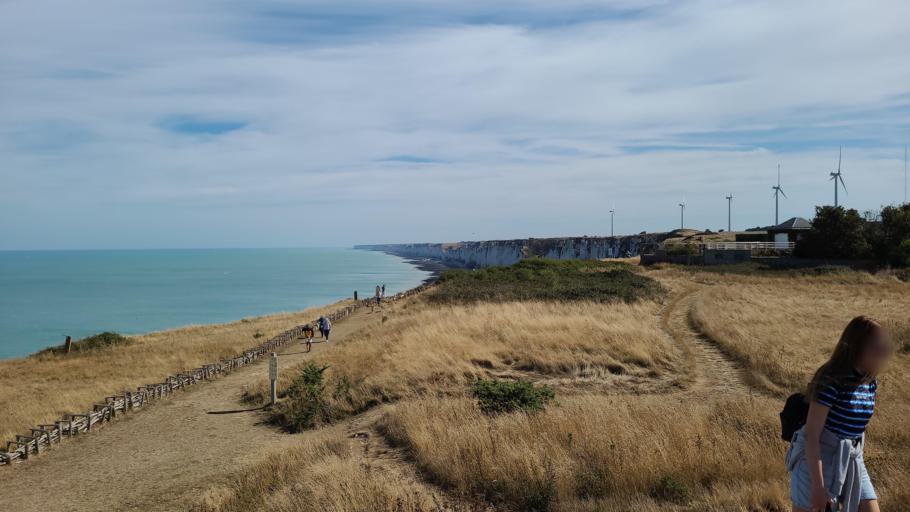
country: FR
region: Haute-Normandie
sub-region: Departement de la Seine-Maritime
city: Fecamp
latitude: 49.7680
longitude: 0.3694
